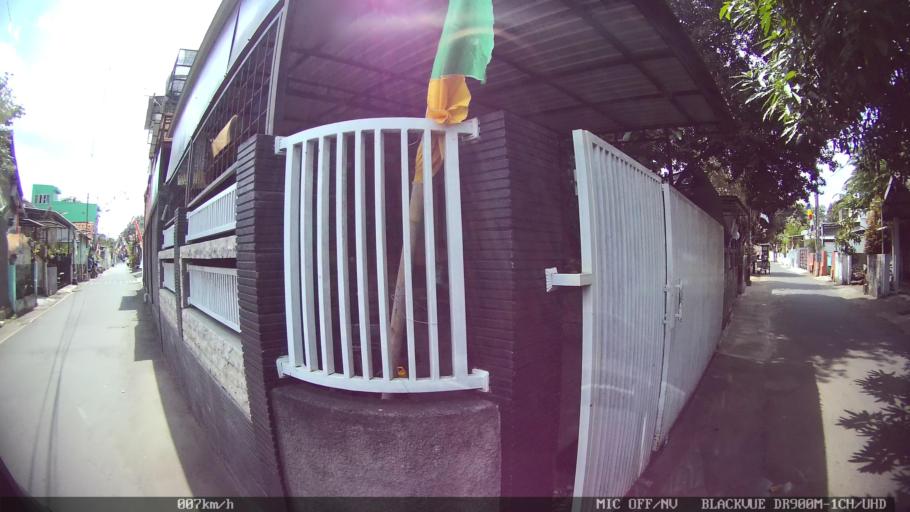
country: ID
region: Daerah Istimewa Yogyakarta
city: Gamping Lor
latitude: -7.8060
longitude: 110.3461
